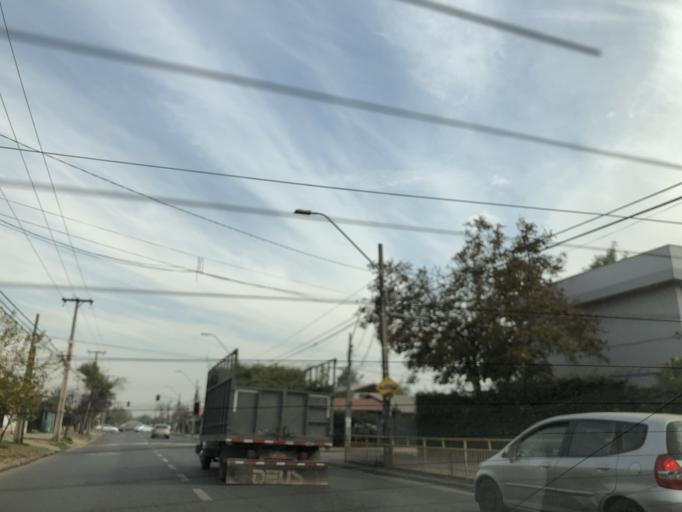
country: CL
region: Santiago Metropolitan
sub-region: Provincia de Cordillera
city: Puente Alto
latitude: -33.5673
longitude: -70.5653
